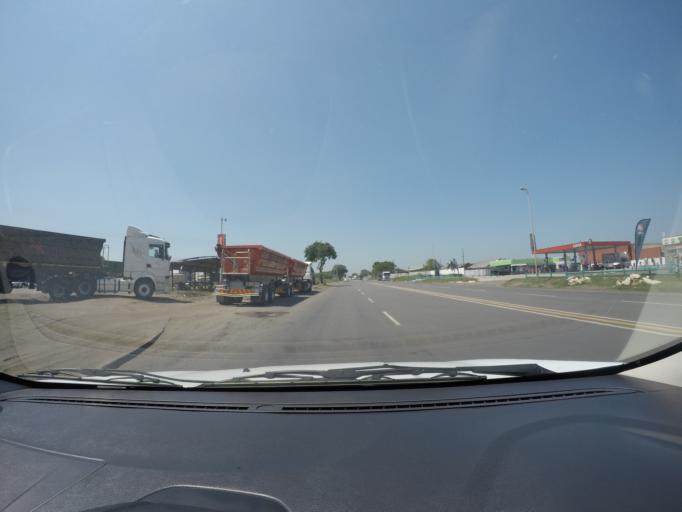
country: ZA
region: KwaZulu-Natal
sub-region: uThungulu District Municipality
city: Richards Bay
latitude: -28.7609
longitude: 32.0225
